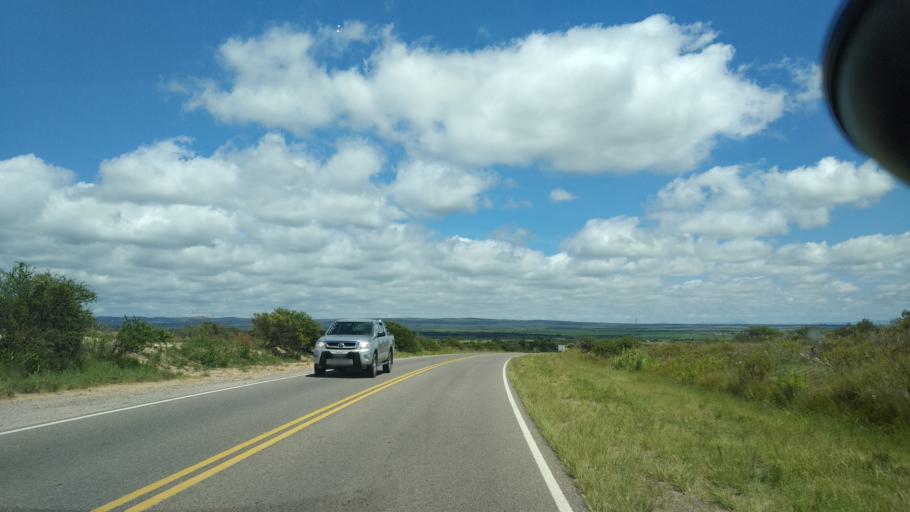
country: AR
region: Cordoba
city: Villa Cura Brochero
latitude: -31.6903
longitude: -65.0718
